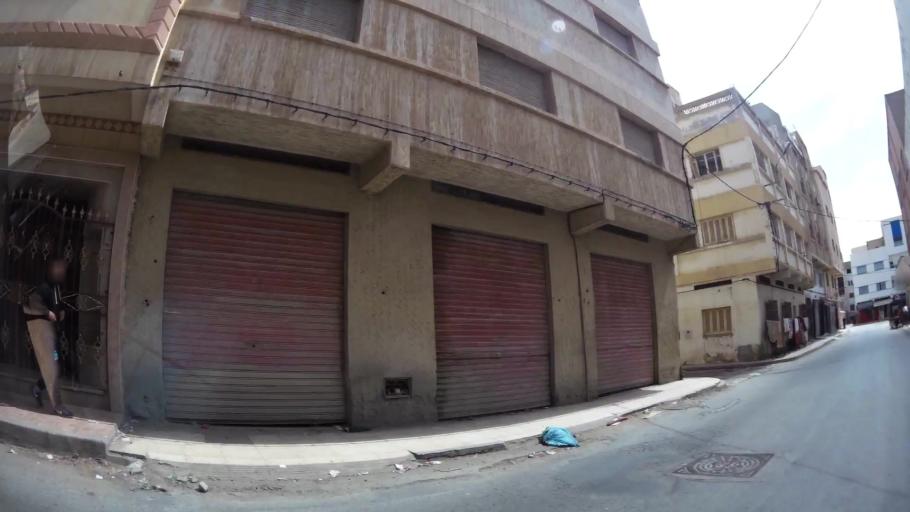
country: MA
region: Oriental
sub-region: Nador
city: Nador
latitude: 35.1674
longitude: -2.9317
